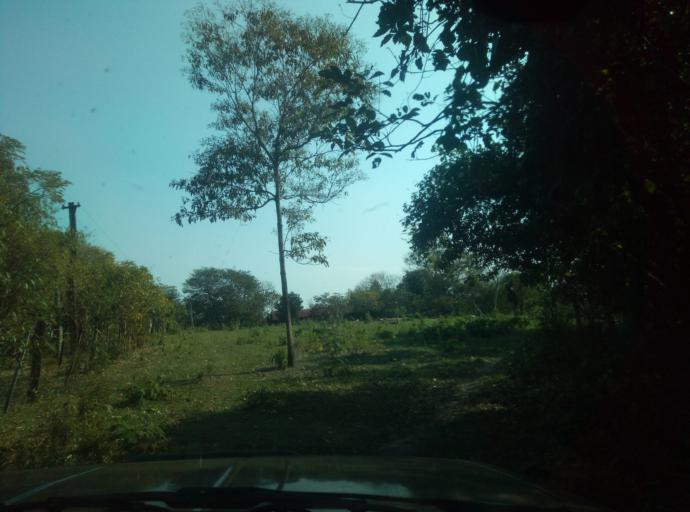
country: PY
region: Caaguazu
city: San Joaquin
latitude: -25.1581
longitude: -56.1301
